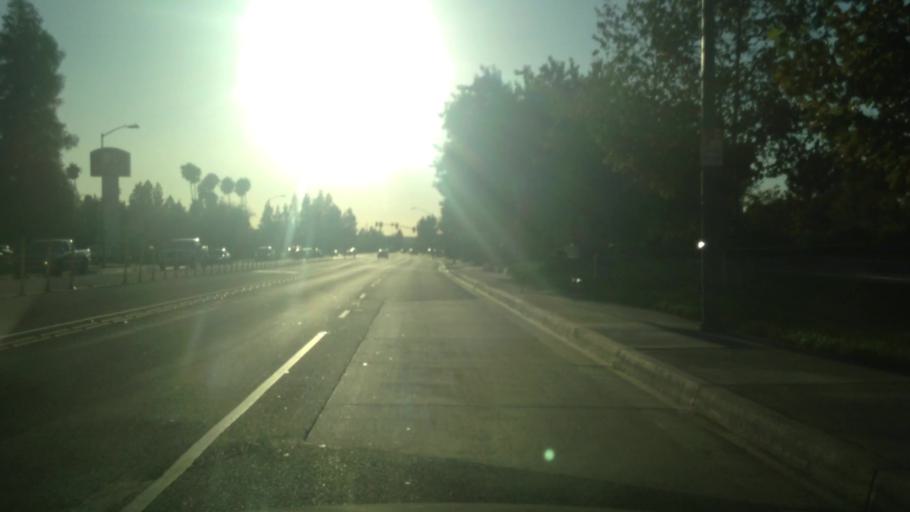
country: US
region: California
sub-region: San Bernardino County
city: Loma Linda
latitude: 34.0659
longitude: -117.2802
